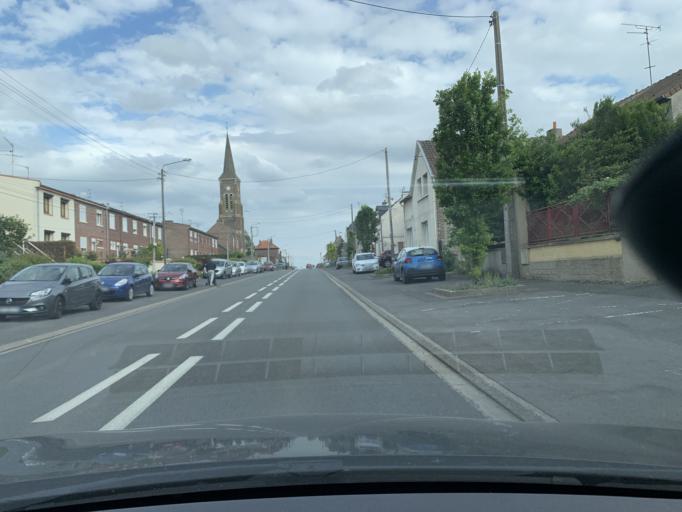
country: FR
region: Nord-Pas-de-Calais
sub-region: Departement du Nord
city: Proville
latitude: 50.1832
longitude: 3.1964
